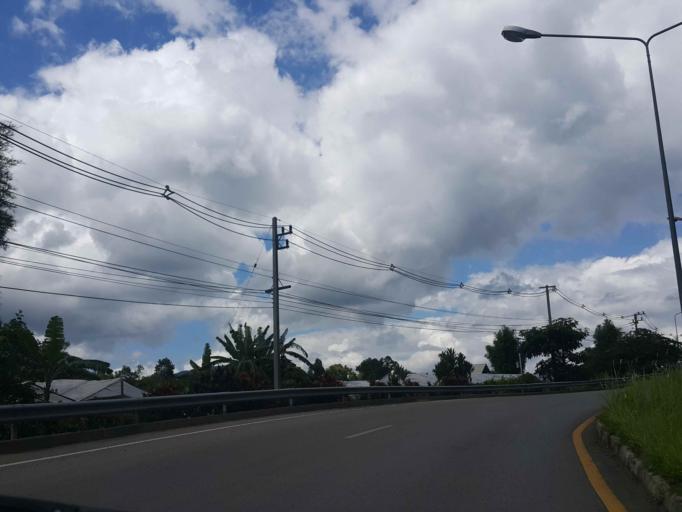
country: TH
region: Chiang Mai
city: Samoeng
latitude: 18.8771
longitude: 98.8013
